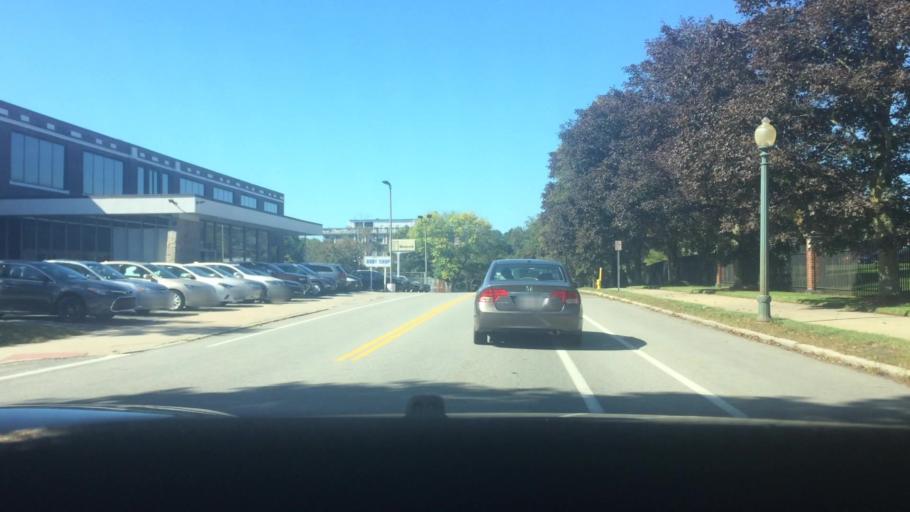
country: US
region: Massachusetts
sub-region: Essex County
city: Andover
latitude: 42.6732
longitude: -71.1453
